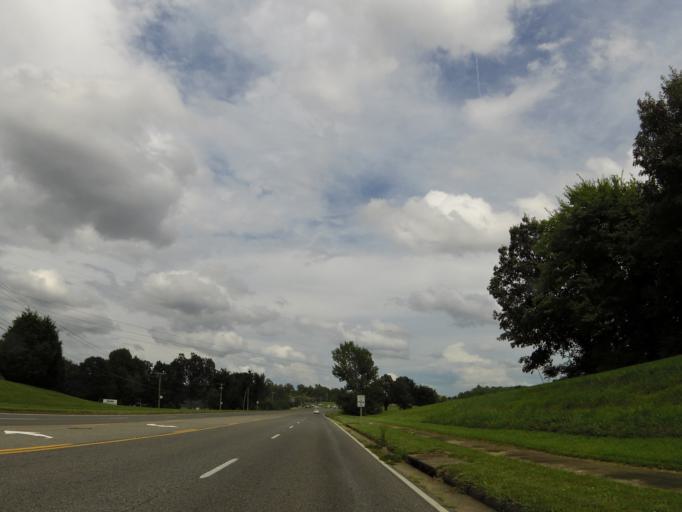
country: US
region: Kentucky
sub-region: McCracken County
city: Hendron
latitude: 37.0499
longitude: -88.6782
